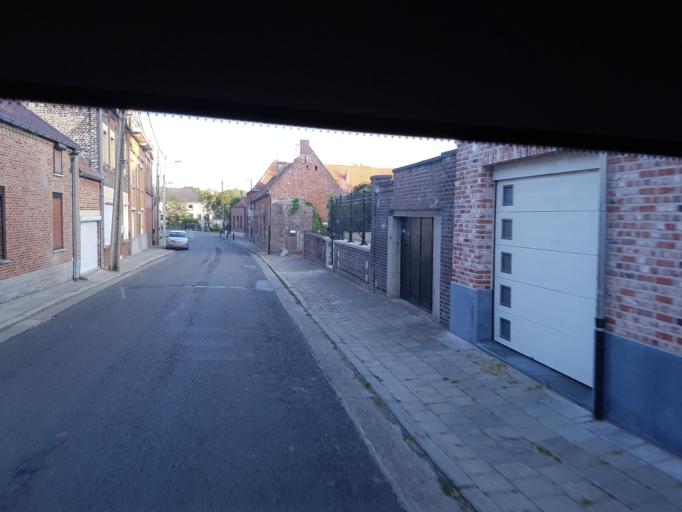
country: FR
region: Nord-Pas-de-Calais
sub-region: Departement du Nord
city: Hergnies
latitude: 50.5078
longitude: 3.5330
